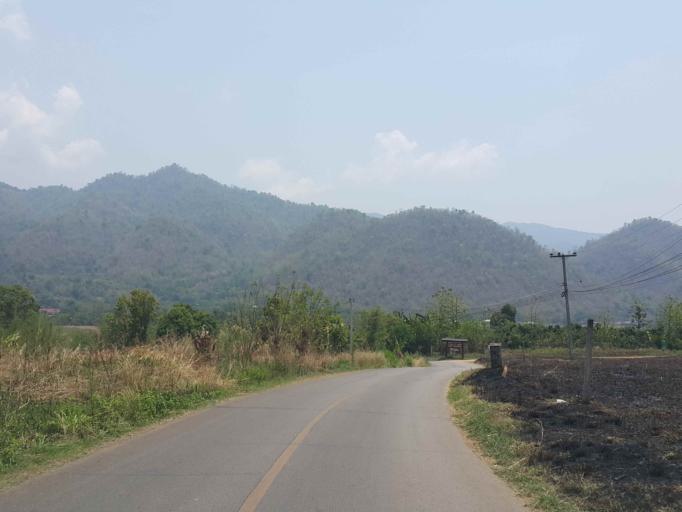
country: TH
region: Chiang Mai
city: Mae Taeng
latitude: 19.2061
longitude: 98.8535
